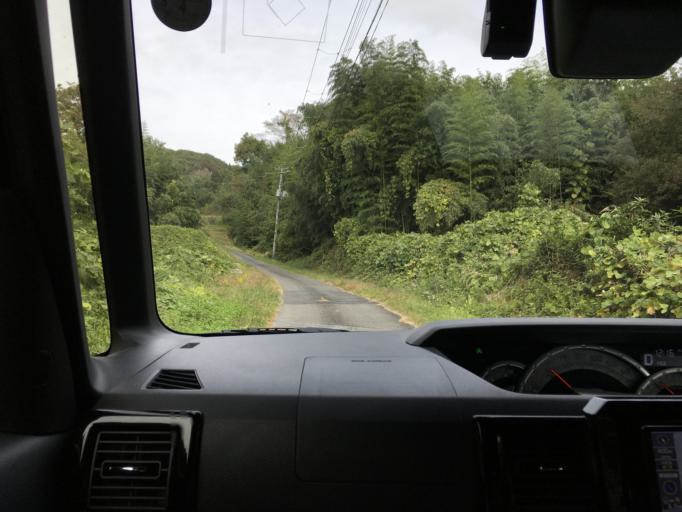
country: JP
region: Iwate
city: Mizusawa
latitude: 39.0274
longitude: 141.3570
